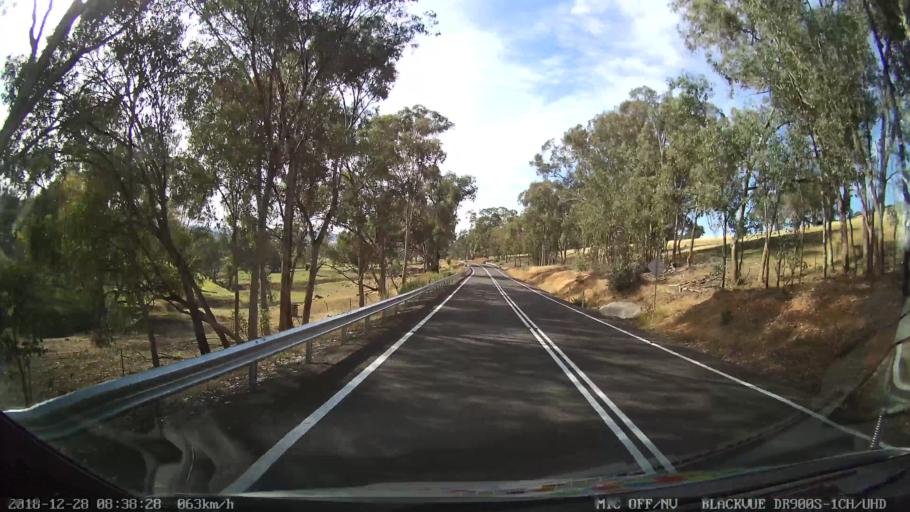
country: AU
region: New South Wales
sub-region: Blayney
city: Blayney
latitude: -34.0039
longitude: 149.3152
